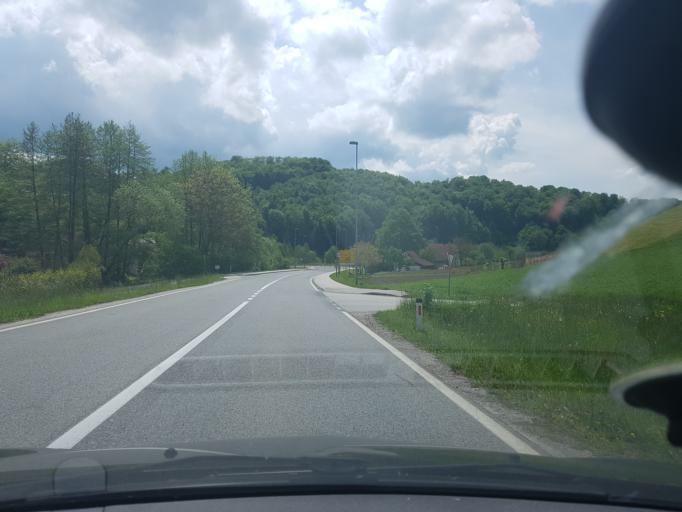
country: SI
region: Rogaska Slatina
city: Rogaska Slatina
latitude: 46.2415
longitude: 15.6051
